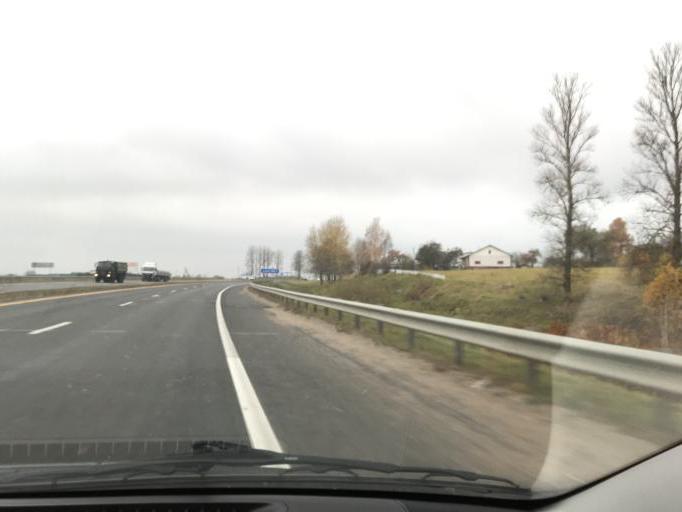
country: BY
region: Vitebsk
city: Vitebsk
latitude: 55.1514
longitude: 30.1165
